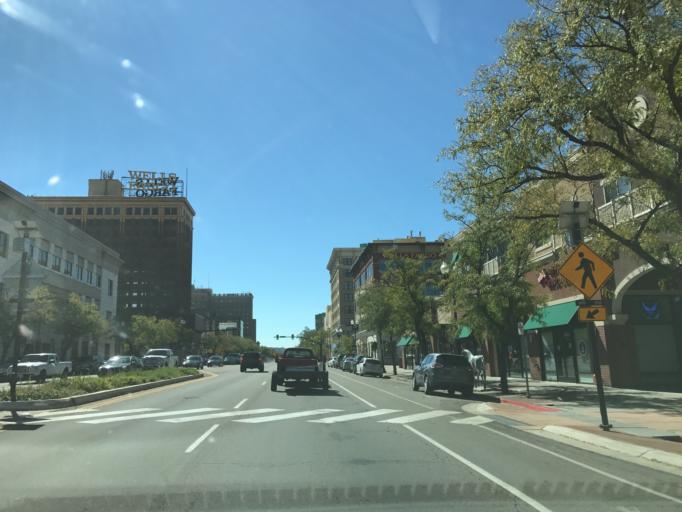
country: US
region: Utah
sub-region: Weber County
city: Ogden
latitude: 41.2240
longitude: -111.9705
